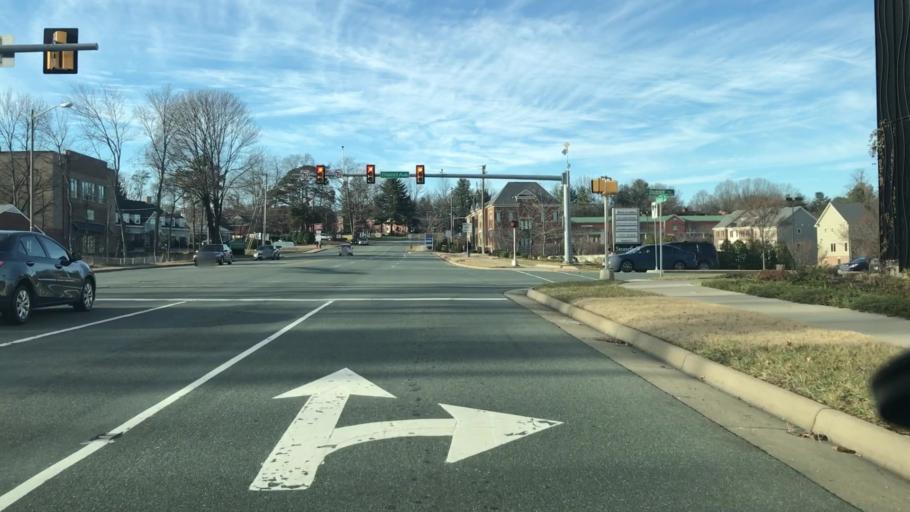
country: US
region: Virginia
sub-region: City of Charlottesville
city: Charlottesville
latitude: 38.0646
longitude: -78.4938
